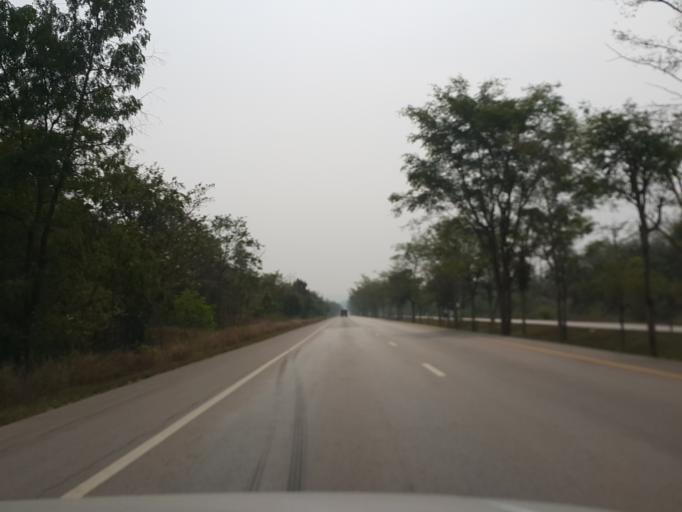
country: TH
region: Lampang
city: Ko Kha
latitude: 18.1199
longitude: 99.3937
